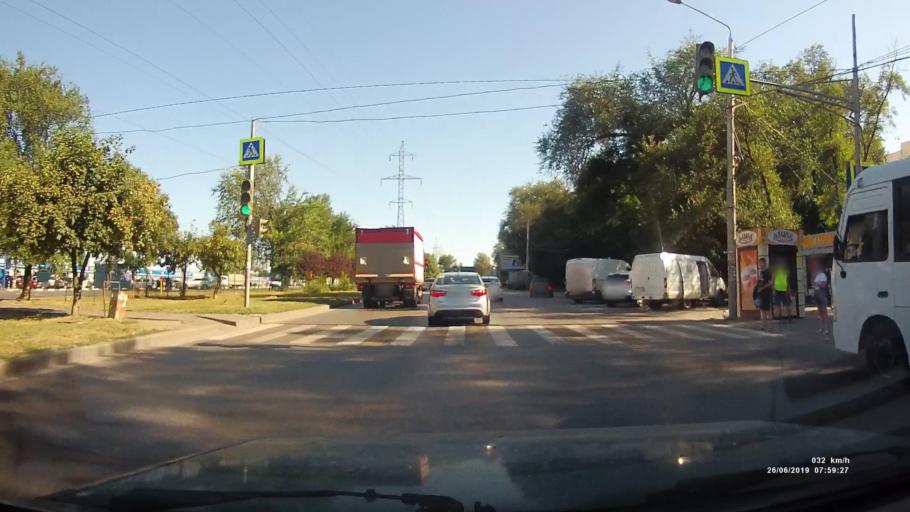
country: RU
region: Rostov
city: Kalinin
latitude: 47.2329
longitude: 39.6139
